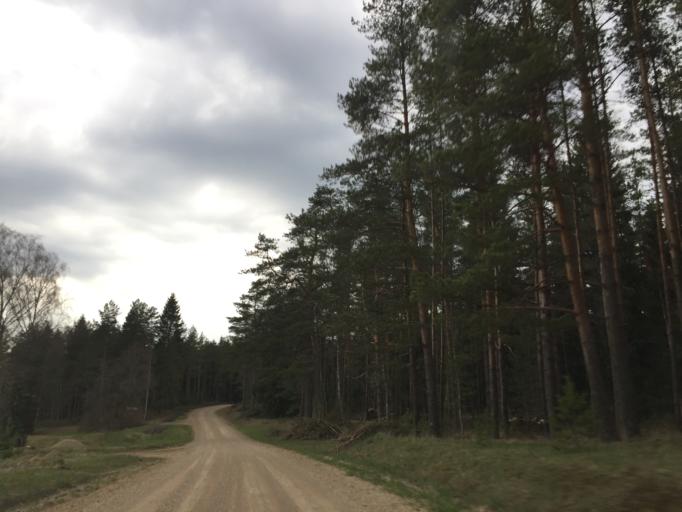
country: EE
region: Vorumaa
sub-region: Antsla vald
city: Vana-Antsla
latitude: 57.9324
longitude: 26.7391
